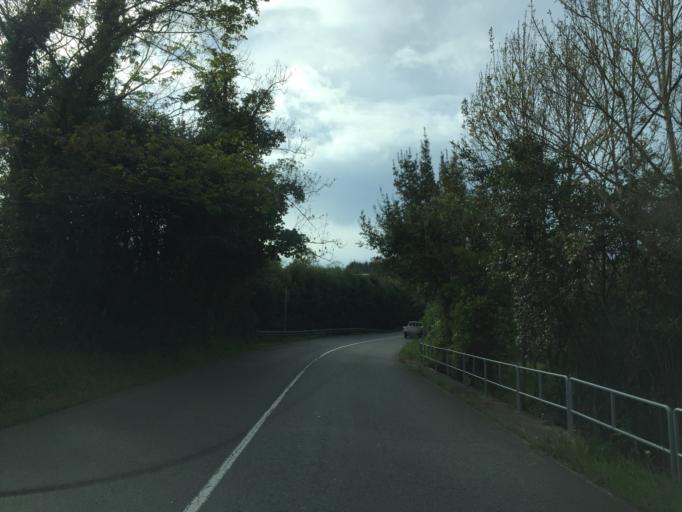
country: ES
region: Asturias
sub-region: Province of Asturias
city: Gijon
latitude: 43.5199
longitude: -5.6091
